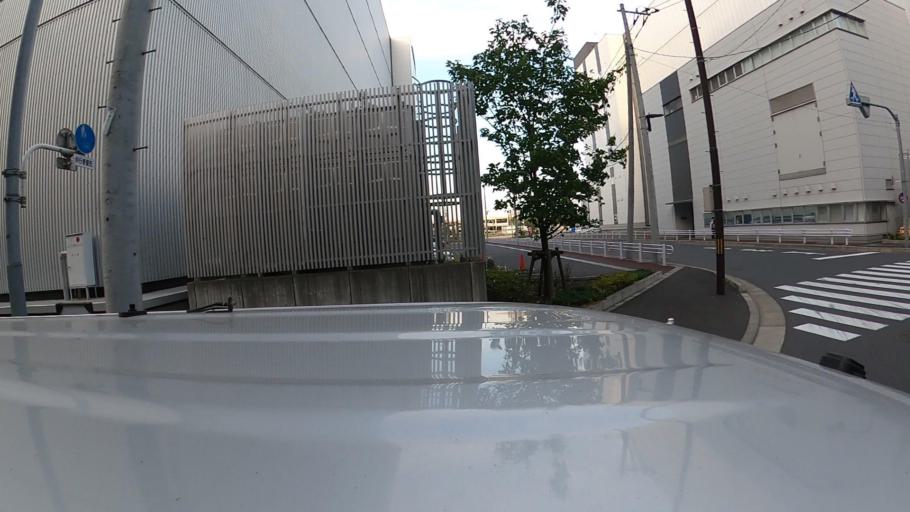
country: JP
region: Kanagawa
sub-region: Kawasaki-shi
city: Kawasaki
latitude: 35.5781
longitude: 139.7526
